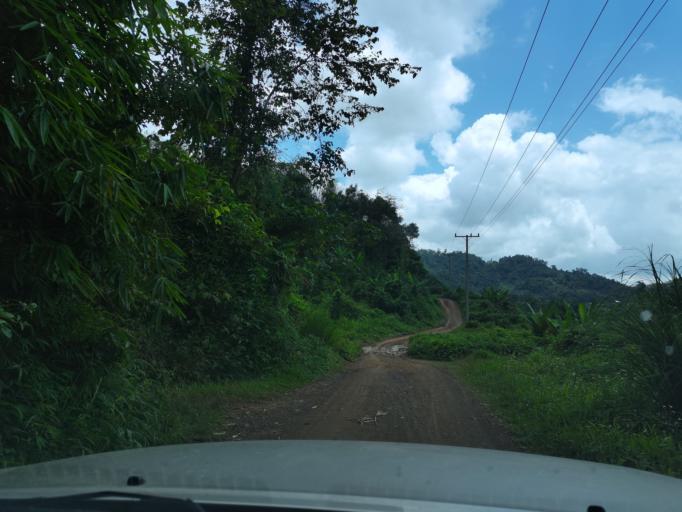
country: LA
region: Loungnamtha
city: Muang Long
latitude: 20.7531
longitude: 101.0181
